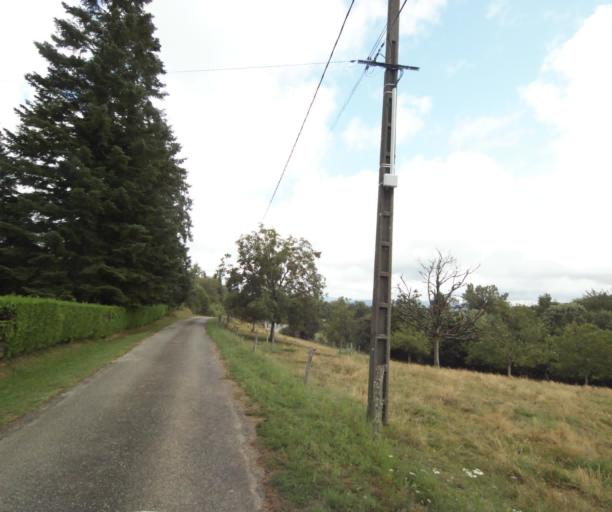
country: FR
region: Limousin
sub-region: Departement de la Correze
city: Sainte-Fortunade
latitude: 45.2011
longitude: 1.8025
